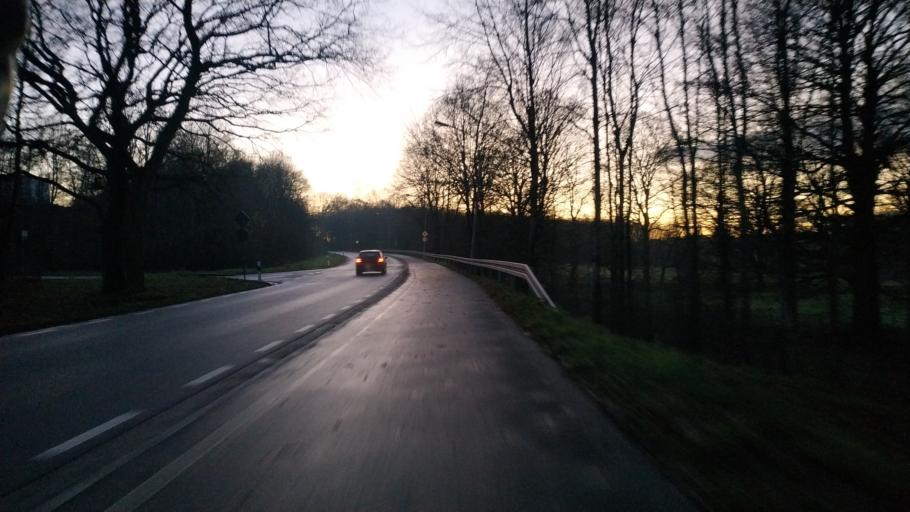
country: DE
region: North Rhine-Westphalia
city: Ibbenburen
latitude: 52.2934
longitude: 7.7366
